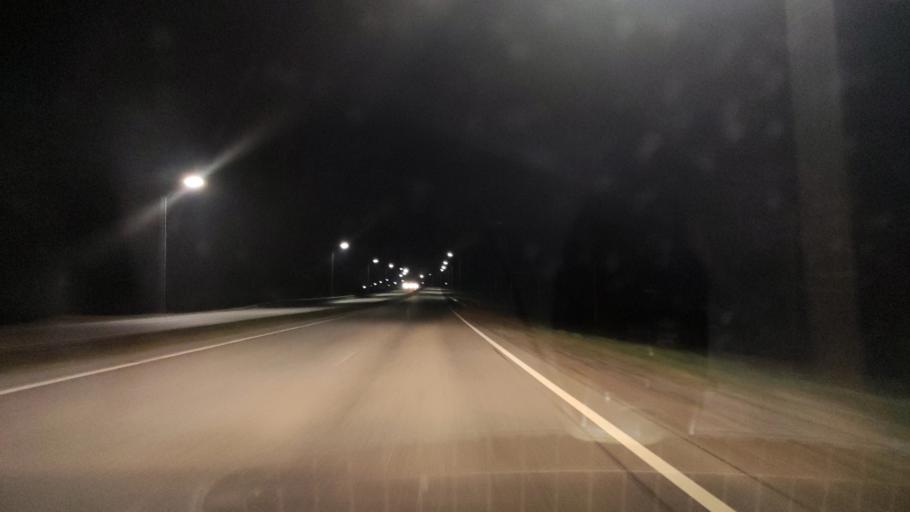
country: RU
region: Belgorod
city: Staryy Oskol
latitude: 51.3912
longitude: 37.8667
